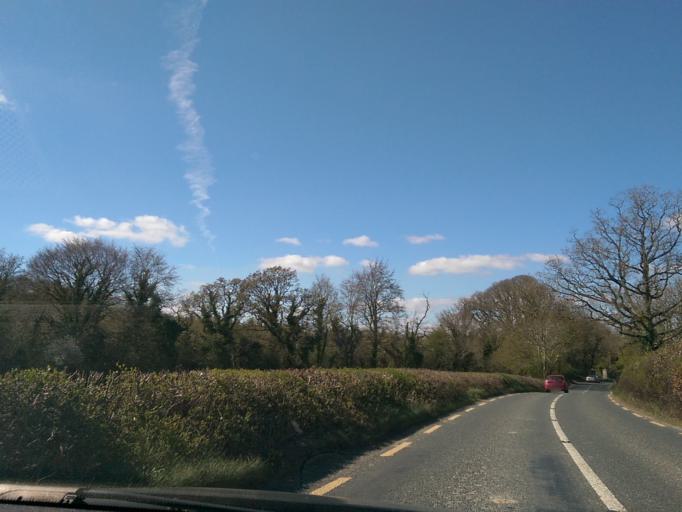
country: IE
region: Leinster
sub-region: Laois
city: Stradbally
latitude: 53.0132
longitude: -7.0850
